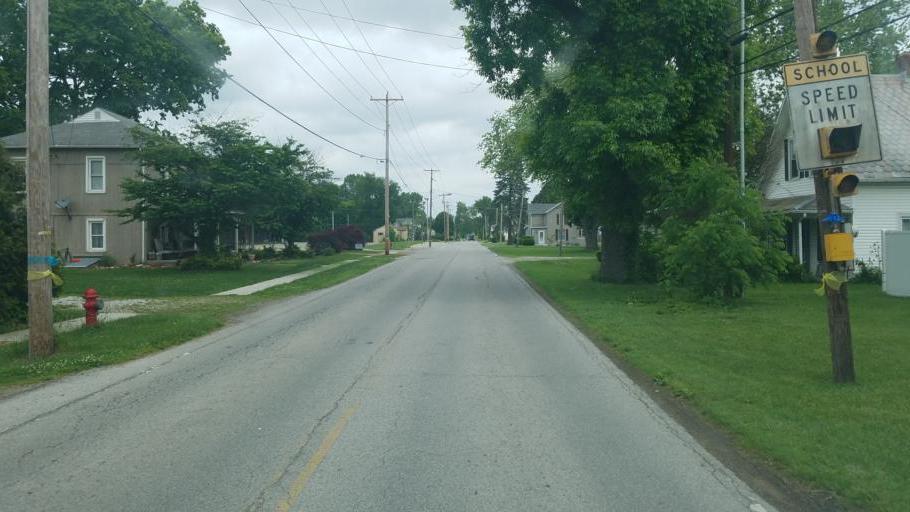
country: US
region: Ohio
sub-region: Licking County
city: Beechwood Trails
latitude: 39.9602
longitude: -82.5991
